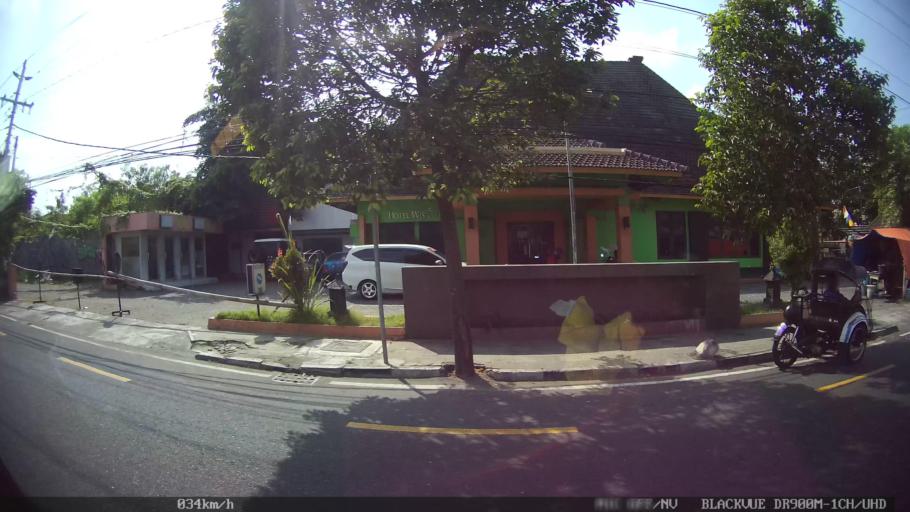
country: ID
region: Daerah Istimewa Yogyakarta
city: Yogyakarta
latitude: -7.8094
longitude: 110.3772
